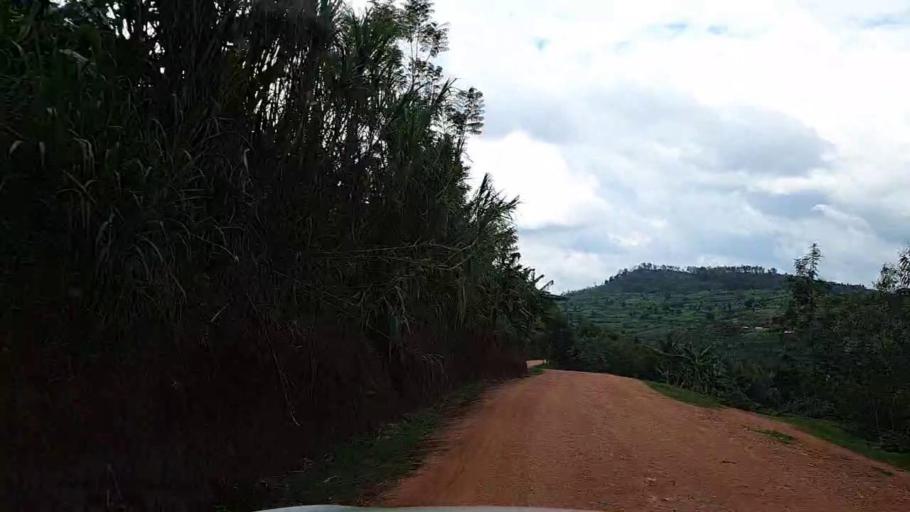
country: RW
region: Southern Province
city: Nyanza
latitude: -2.4124
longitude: 29.6725
